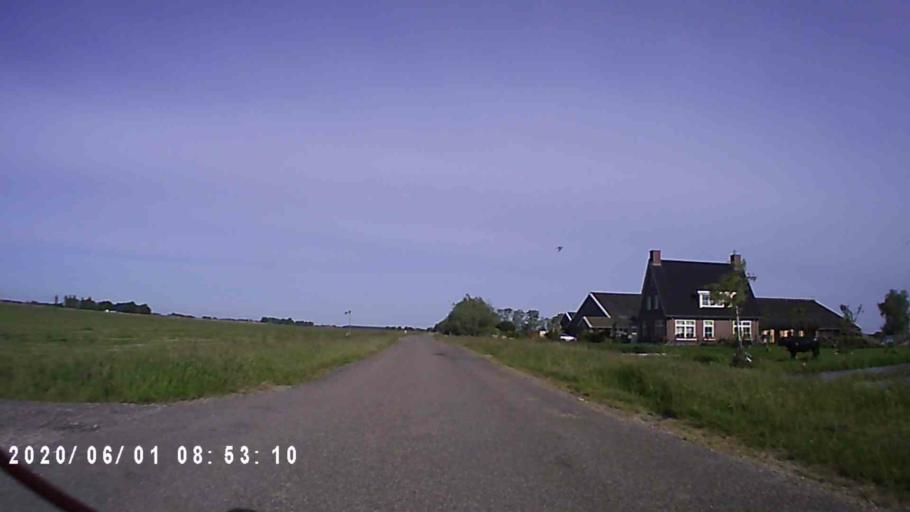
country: NL
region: Friesland
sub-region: Gemeente Leeuwarderadeel
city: Britsum
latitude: 53.2780
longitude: 5.8288
